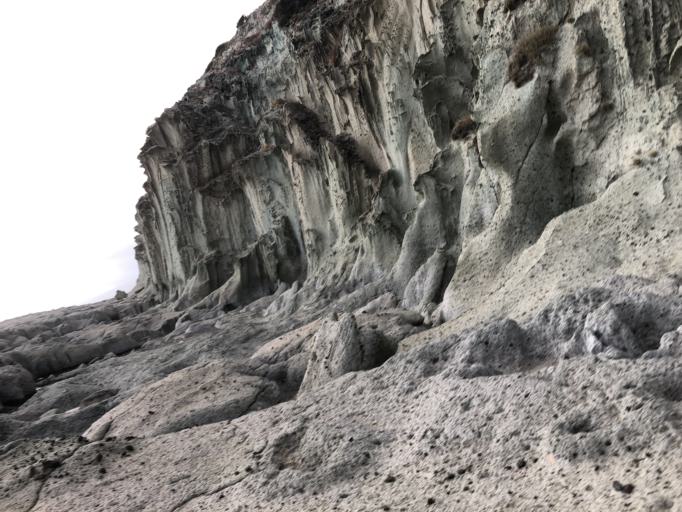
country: IT
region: Sardinia
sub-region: Provincia di Oristano
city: Bosa
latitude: 40.2980
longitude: 8.4686
